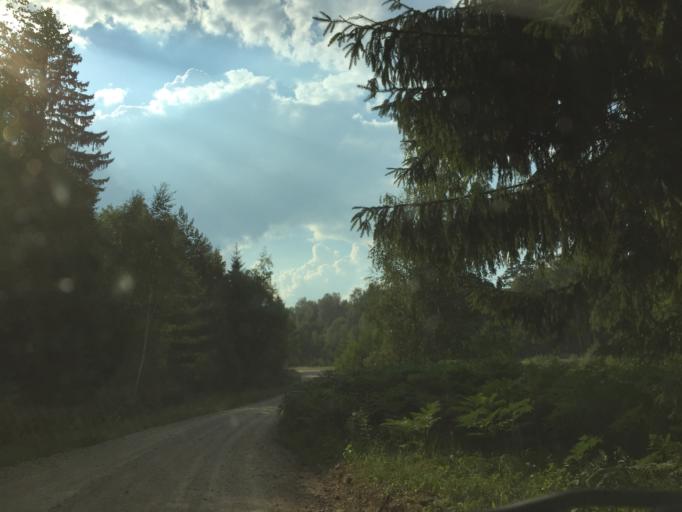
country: LT
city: Zagare
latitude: 56.4477
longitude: 23.1166
